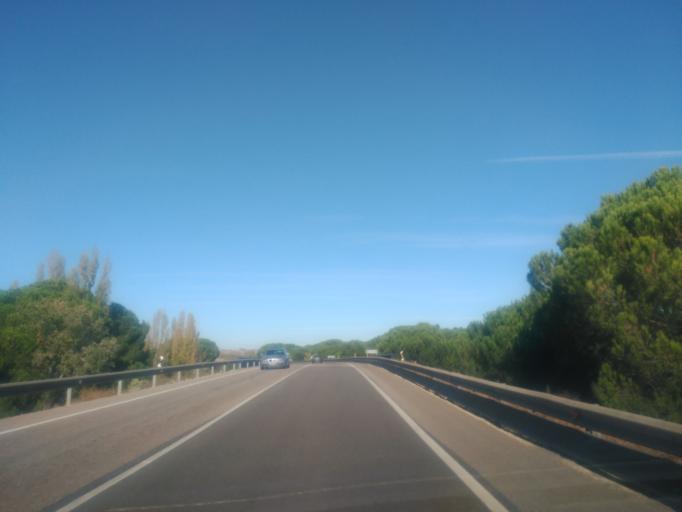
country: ES
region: Castille and Leon
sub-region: Provincia de Valladolid
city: Penafiel
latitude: 41.6060
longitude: -4.1407
